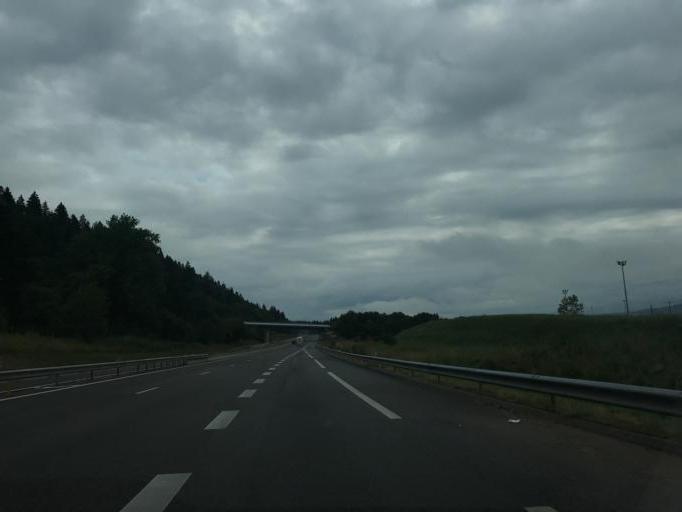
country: FR
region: Rhone-Alpes
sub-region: Departement de l'Ain
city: Bellignat
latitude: 46.2377
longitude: 5.6185
